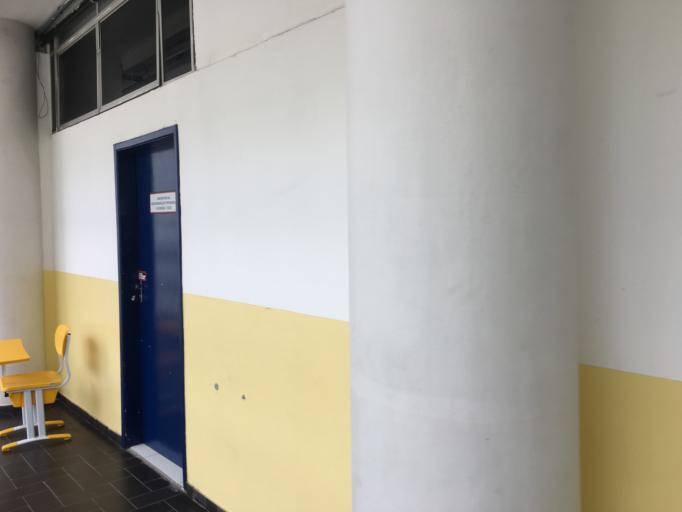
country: BR
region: Bahia
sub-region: Salvador
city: Salvador
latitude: -12.9995
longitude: -38.5105
